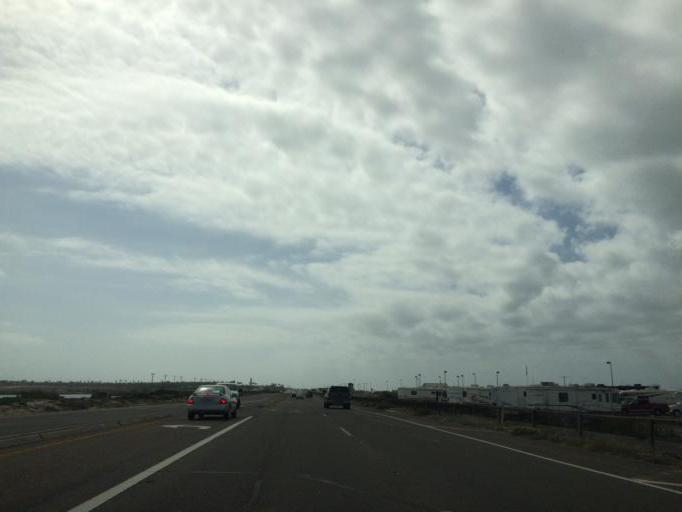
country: US
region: California
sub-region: Orange County
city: Huntington Beach
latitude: 33.6919
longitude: -118.0438
